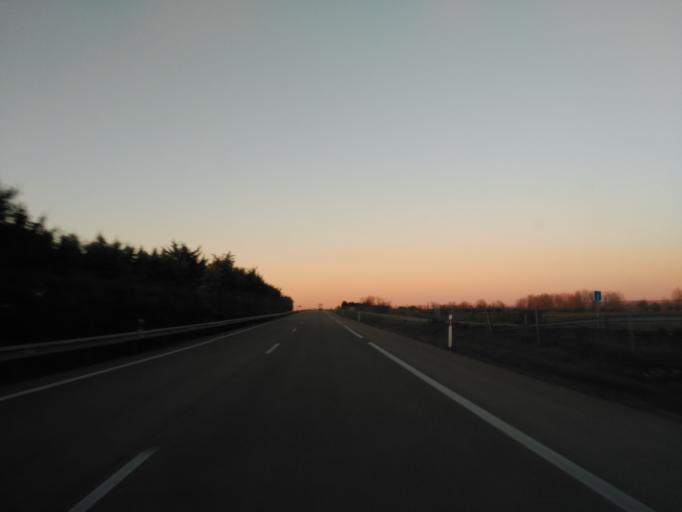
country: ES
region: Castille and Leon
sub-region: Provincia de Valladolid
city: Cubillas de Santa Marta
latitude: 41.7792
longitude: -4.6152
